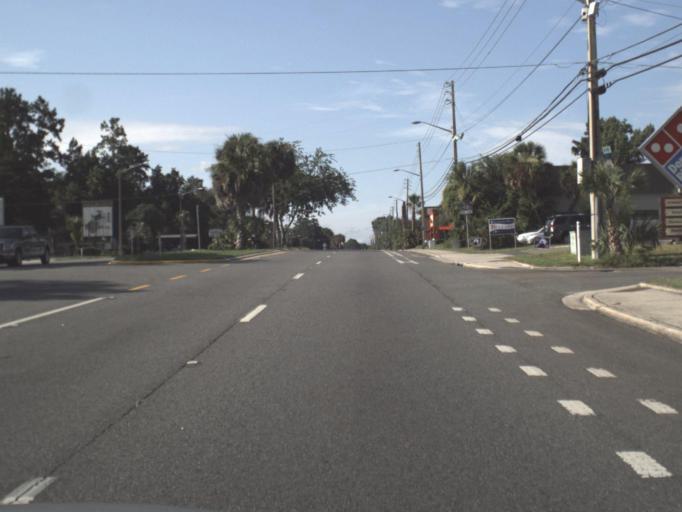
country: US
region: Florida
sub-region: Alachua County
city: Gainesville
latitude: 29.6331
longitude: -82.3395
